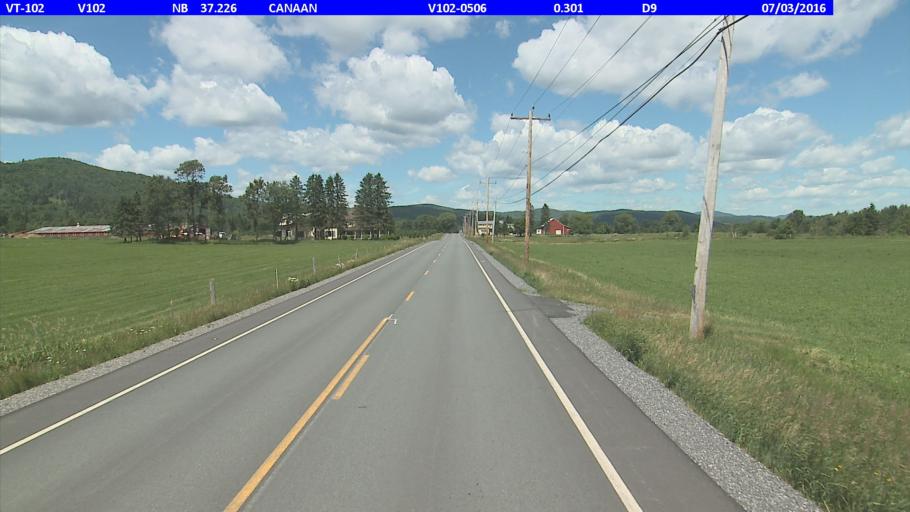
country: US
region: New Hampshire
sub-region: Coos County
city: Colebrook
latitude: 44.9144
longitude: -71.5105
